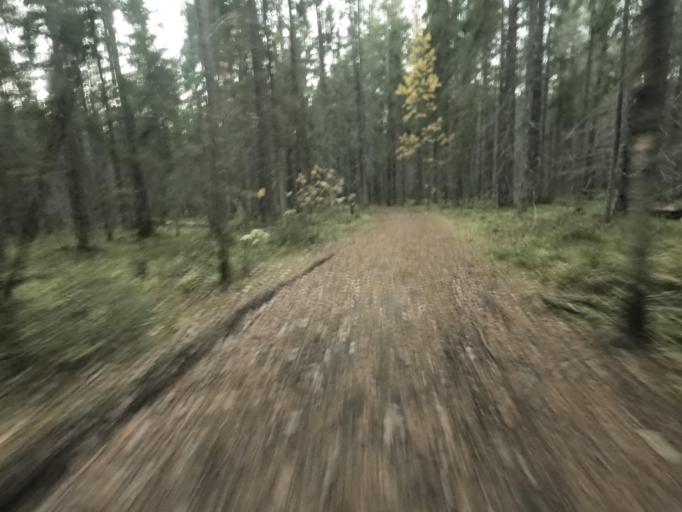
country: RU
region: Leningrad
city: Leninskoye
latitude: 60.1993
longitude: 29.8384
